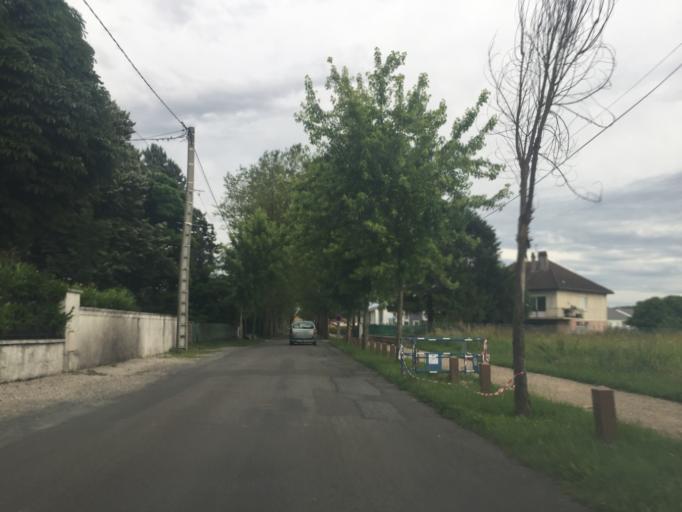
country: FR
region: Rhone-Alpes
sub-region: Departement de l'Ain
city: Thil
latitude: 45.8225
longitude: 5.0165
